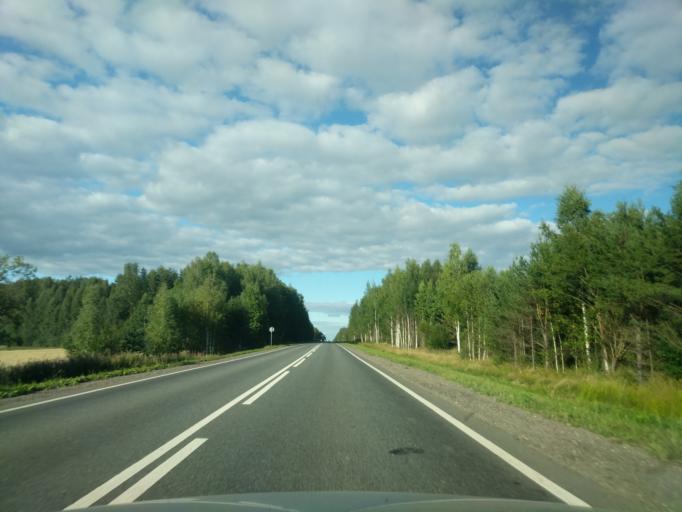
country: RU
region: Kostroma
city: Manturovo
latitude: 58.2090
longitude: 44.6031
